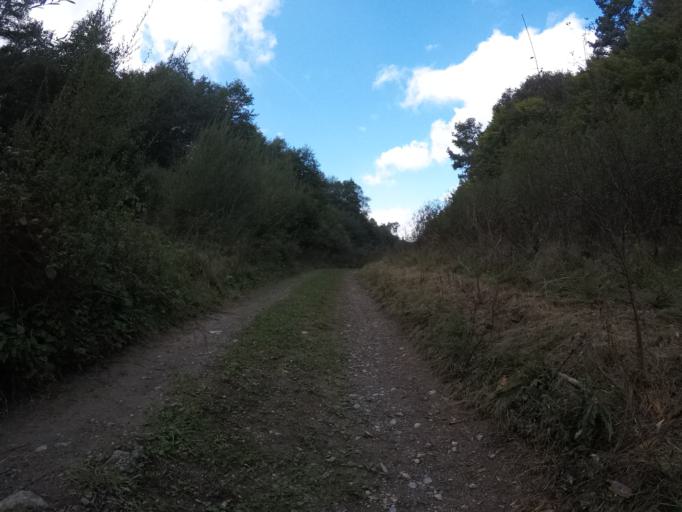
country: SK
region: Presovsky
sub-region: Okres Presov
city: Presov
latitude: 48.9298
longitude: 21.1708
